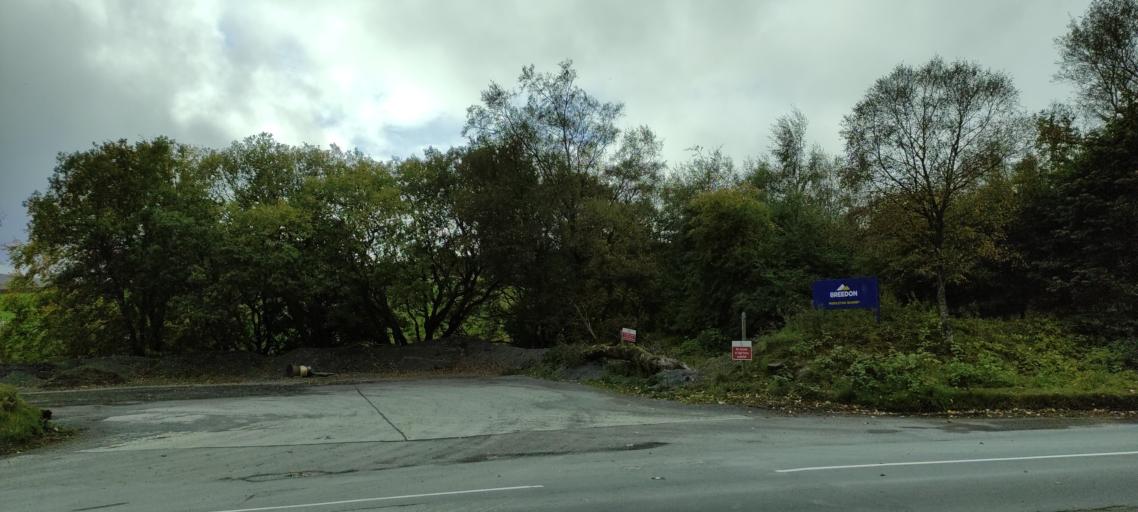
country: GB
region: England
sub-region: County Durham
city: Holwick
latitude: 54.6553
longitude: -2.1885
